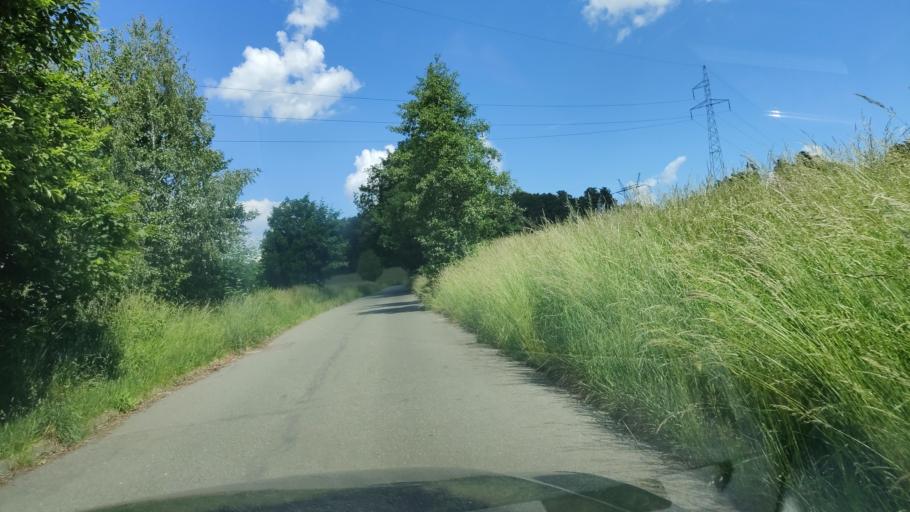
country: PL
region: Lower Silesian Voivodeship
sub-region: Powiat swidnicki
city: Swiebodzice
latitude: 50.8335
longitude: 16.3044
